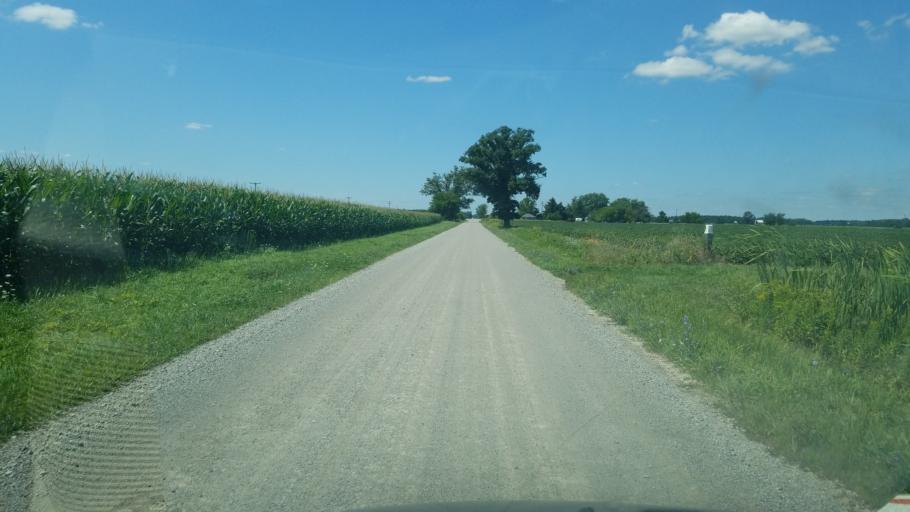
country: US
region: Ohio
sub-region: Fulton County
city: Delta
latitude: 41.7279
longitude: -84.0326
